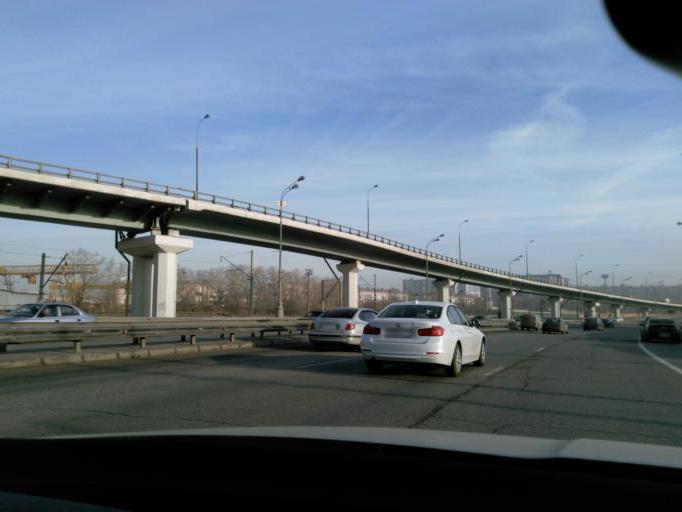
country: RU
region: Moskovskaya
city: Presnenskiy
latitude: 55.7668
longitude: 37.5379
